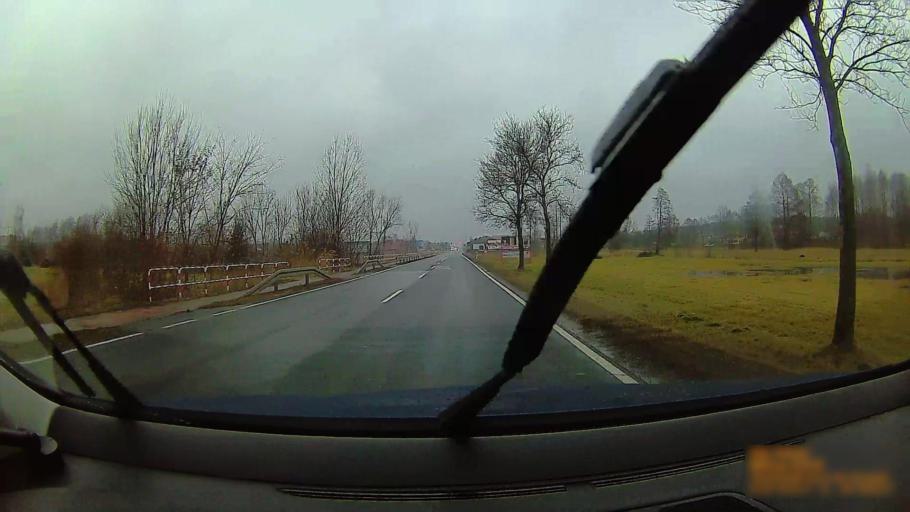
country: PL
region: Greater Poland Voivodeship
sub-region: Konin
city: Konin
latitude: 52.1729
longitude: 18.2729
